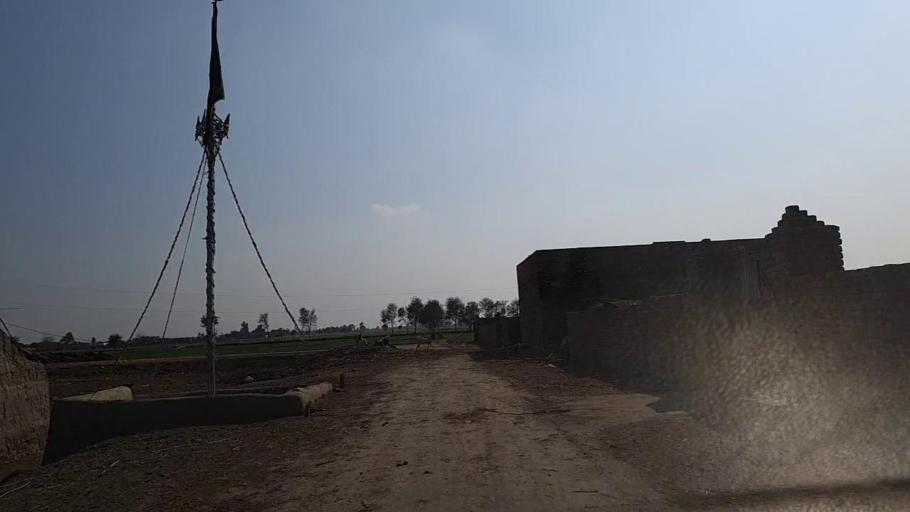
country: PK
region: Sindh
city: Jam Sahib
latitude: 26.2997
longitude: 68.5698
